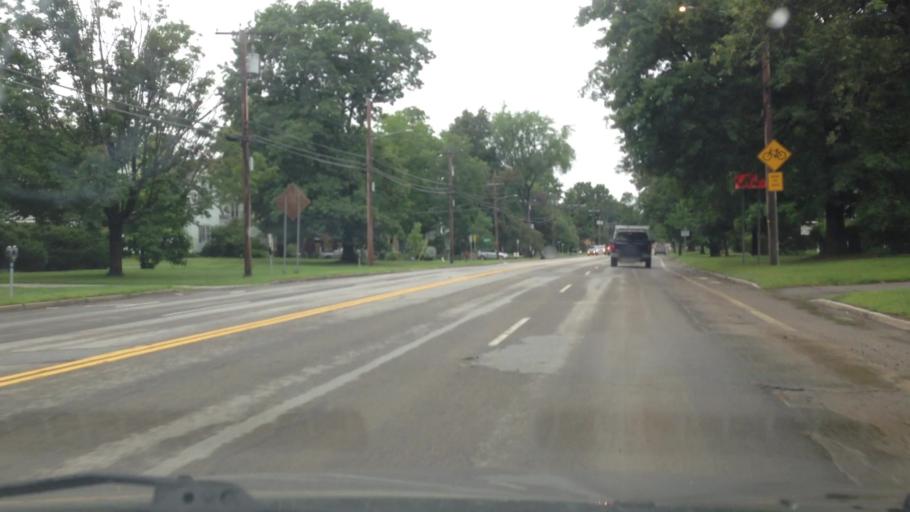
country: US
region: New Hampshire
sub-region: Cheshire County
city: Keene
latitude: 42.9237
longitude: -72.2767
